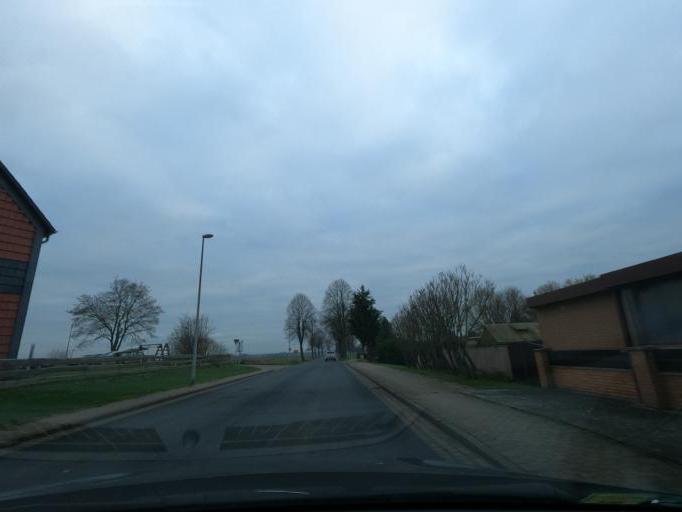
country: DE
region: Lower Saxony
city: Remlingen
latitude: 52.1107
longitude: 10.6788
